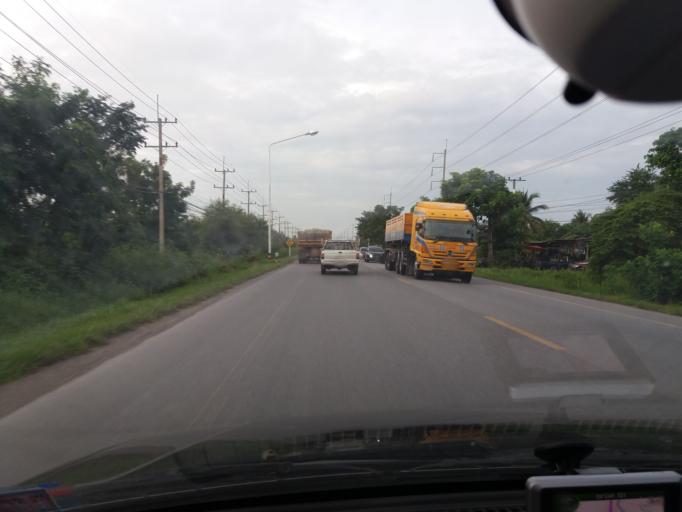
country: TH
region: Suphan Buri
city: U Thong
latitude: 14.4010
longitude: 99.8962
